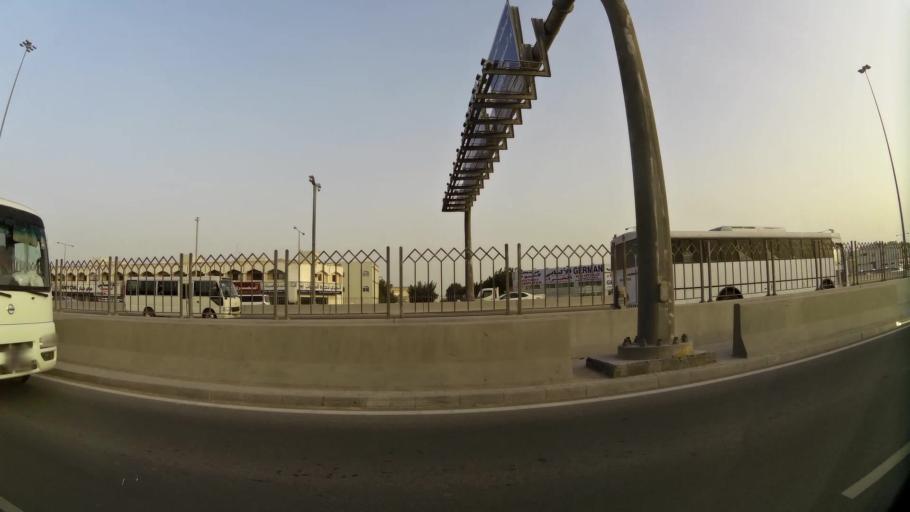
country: QA
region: Baladiyat ar Rayyan
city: Ar Rayyan
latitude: 25.2302
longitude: 51.4396
